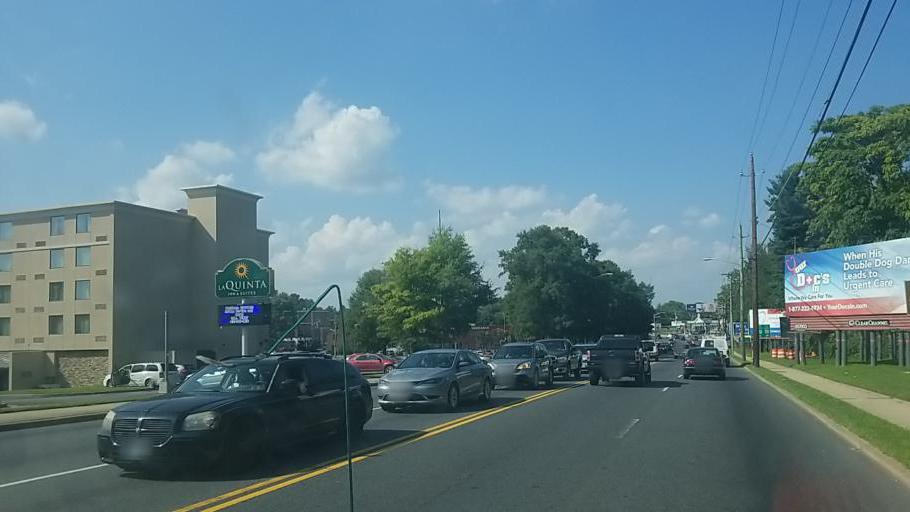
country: US
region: Maryland
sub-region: Wicomico County
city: Salisbury
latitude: 38.3634
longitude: -75.5960
